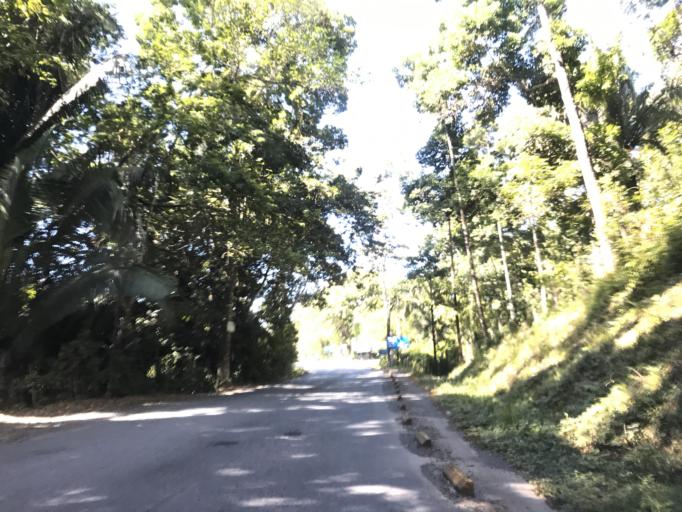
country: GT
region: Izabal
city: Morales
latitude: 15.6498
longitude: -89.0088
